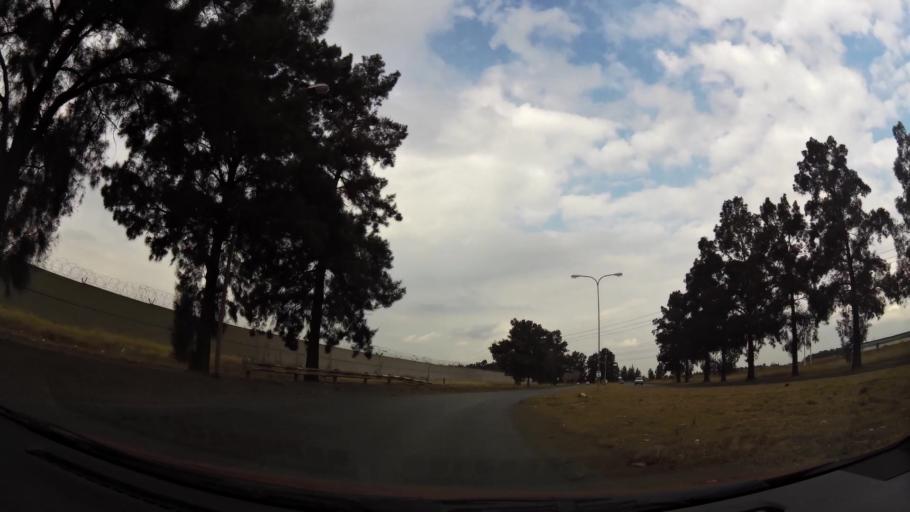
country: ZA
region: Gauteng
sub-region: Sedibeng District Municipality
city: Vanderbijlpark
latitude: -26.6728
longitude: 27.8189
